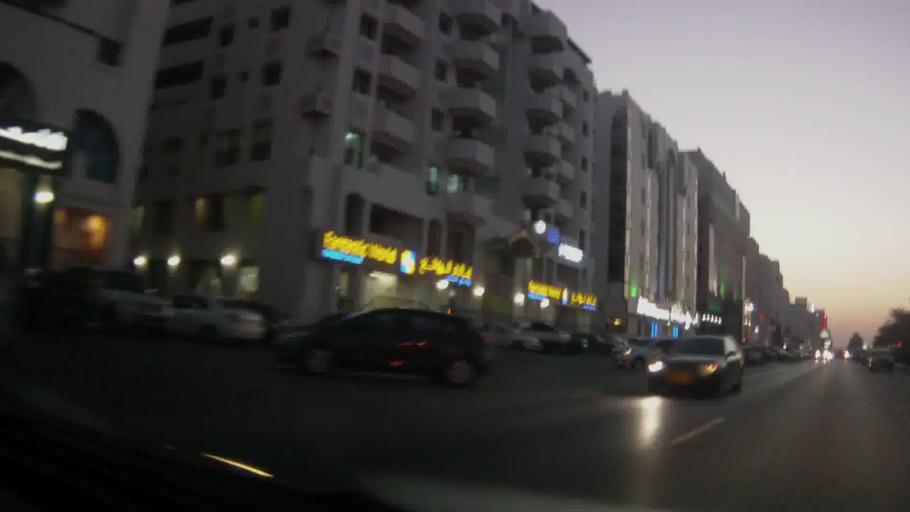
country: OM
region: Muhafazat Masqat
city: Bawshar
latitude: 23.5968
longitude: 58.4310
